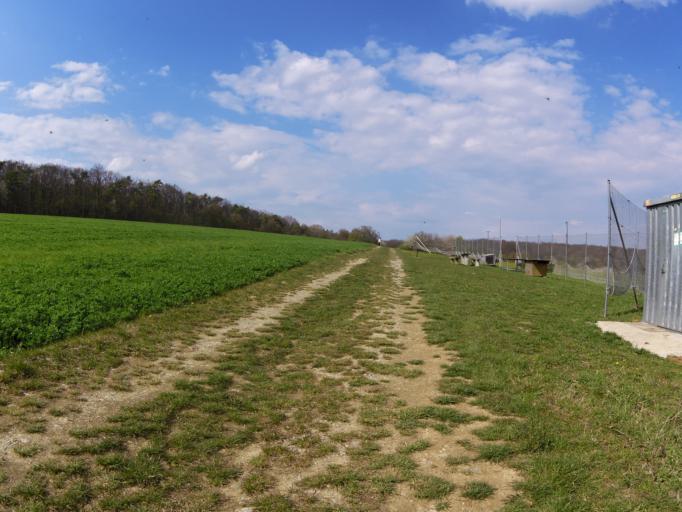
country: DE
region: Bavaria
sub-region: Regierungsbezirk Unterfranken
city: Rimpar
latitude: 49.8712
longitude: 9.9603
